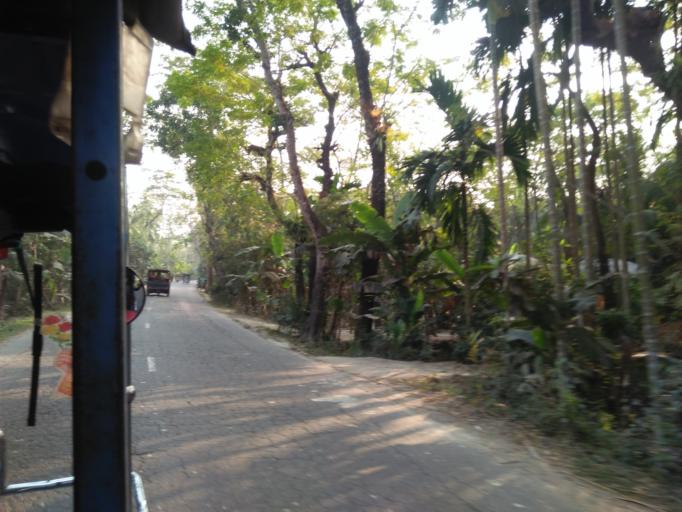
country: BD
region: Barisal
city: Bhola
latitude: 22.7107
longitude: 90.6401
